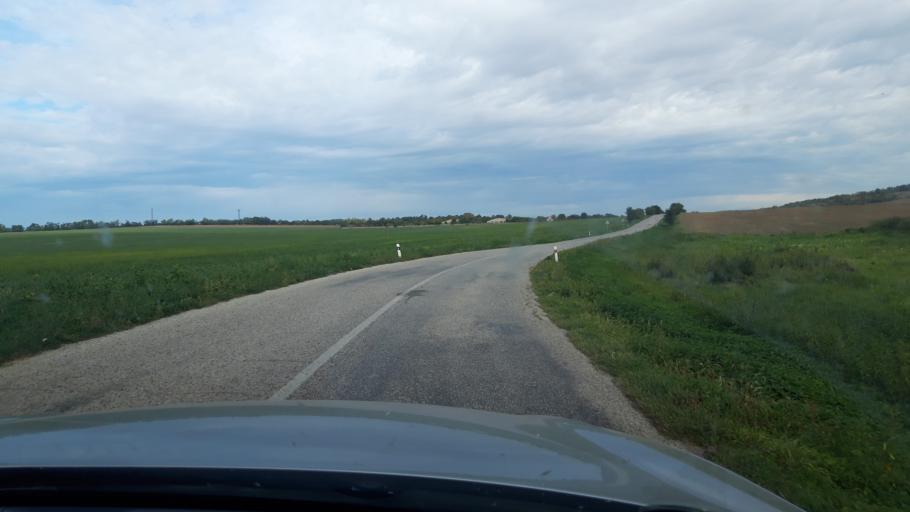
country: SK
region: Nitriansky
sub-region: Okres Nitra
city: Vrable
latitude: 48.1213
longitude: 18.3335
